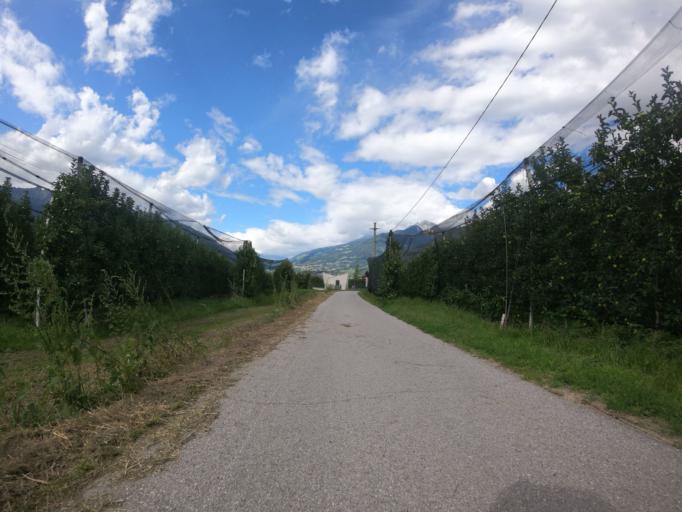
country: IT
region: Trentino-Alto Adige
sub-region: Bolzano
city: Cermes
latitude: 46.6296
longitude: 11.1514
